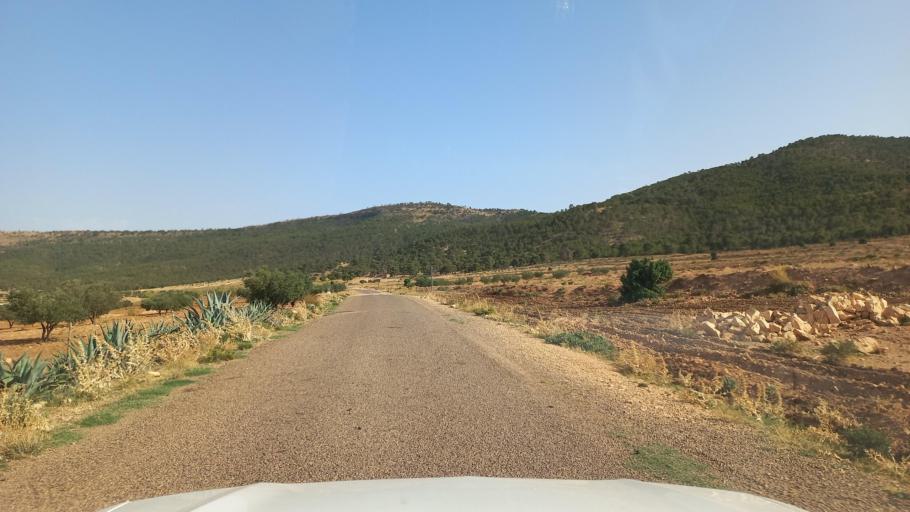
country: TN
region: Al Qasrayn
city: Kasserine
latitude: 35.3384
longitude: 8.8358
